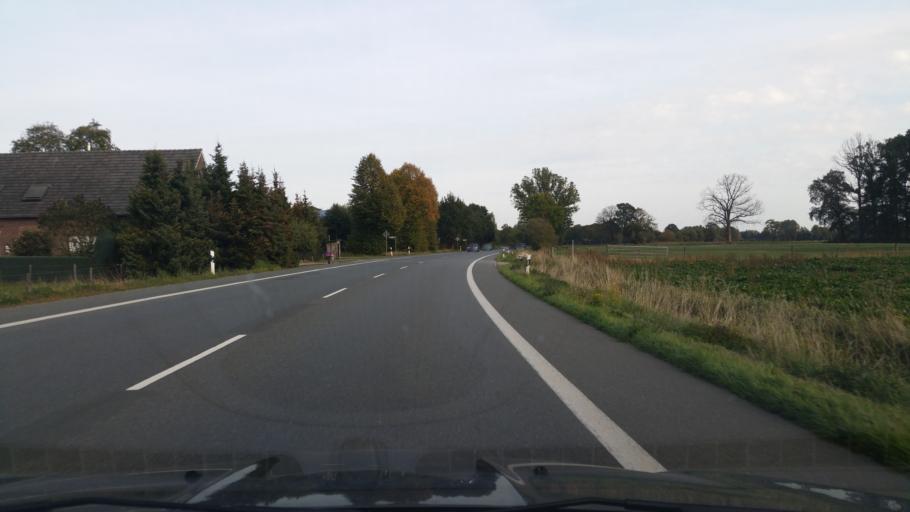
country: DE
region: North Rhine-Westphalia
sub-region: Regierungsbezirk Munster
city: Isselburg
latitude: 51.8625
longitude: 6.5198
